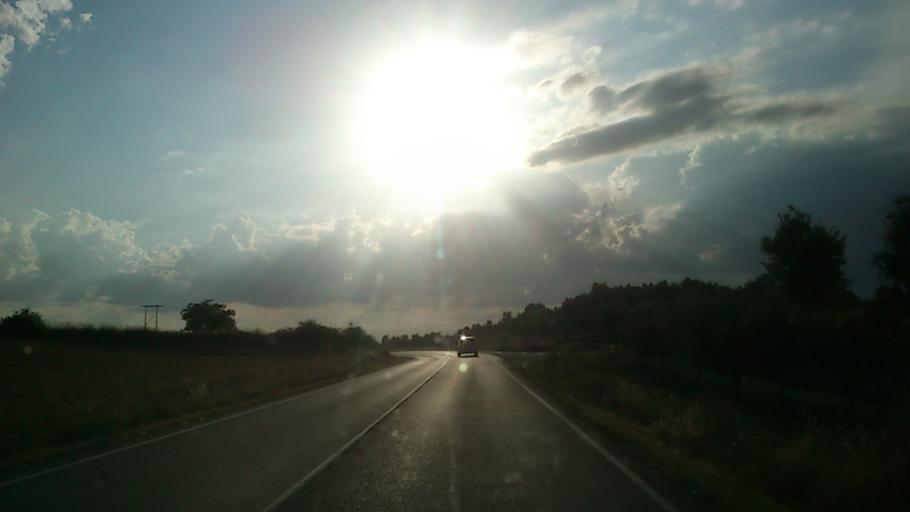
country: ES
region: Castille and Leon
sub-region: Provincia de Burgos
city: Frias
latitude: 42.7910
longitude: -3.2803
